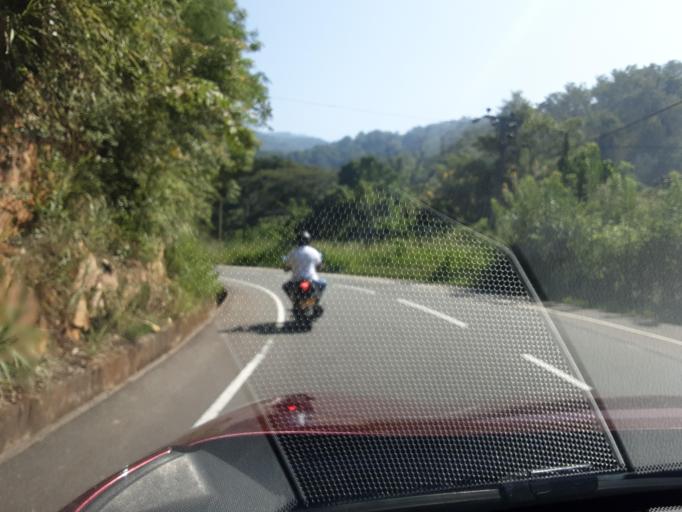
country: LK
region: Uva
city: Badulla
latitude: 7.0405
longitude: 81.0597
